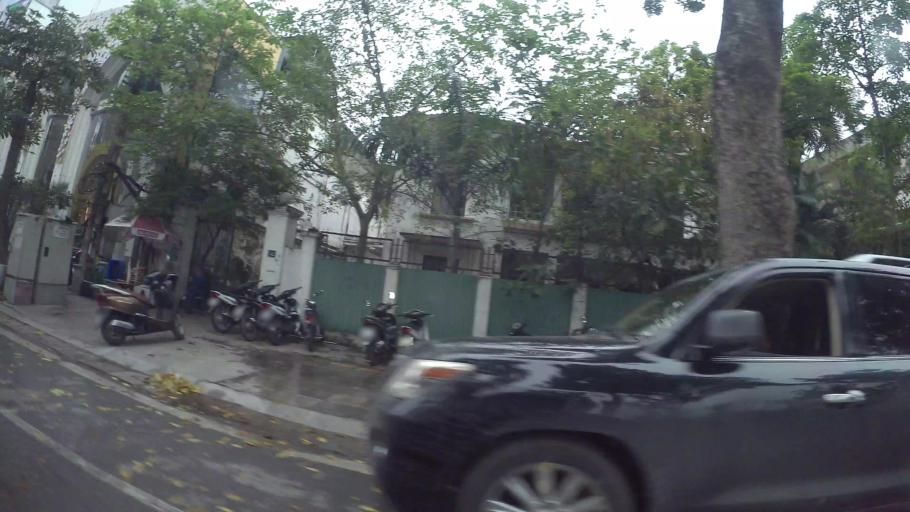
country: VN
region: Ha Noi
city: Hai BaTrung
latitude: 21.0194
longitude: 105.8462
